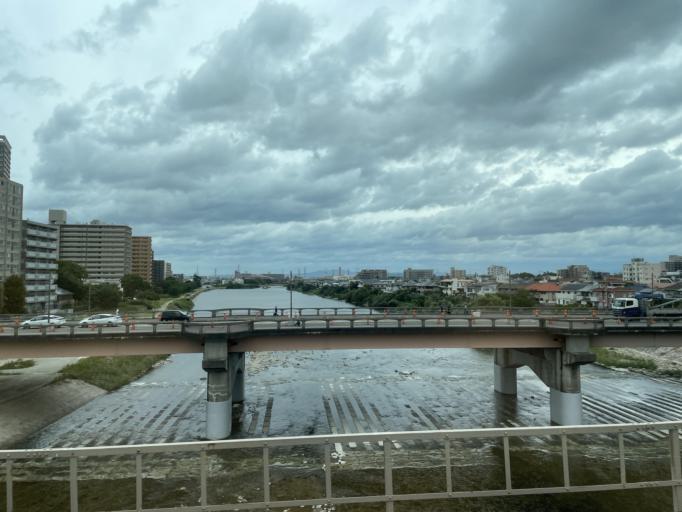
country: JP
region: Hyogo
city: Takarazuka
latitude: 34.8060
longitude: 135.3466
